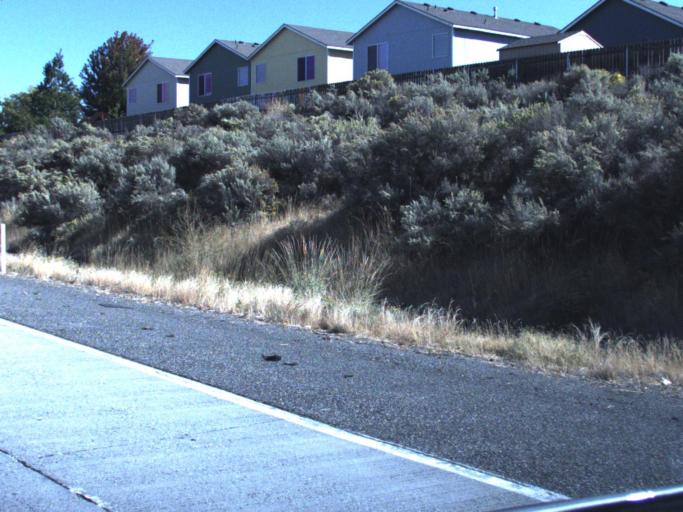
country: US
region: Washington
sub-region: Benton County
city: Richland
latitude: 46.2525
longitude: -119.3099
